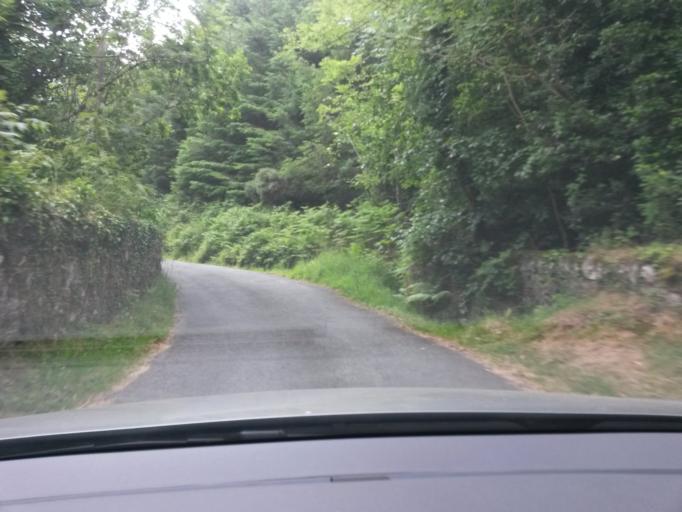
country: IE
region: Leinster
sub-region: Wicklow
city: Enniskerry
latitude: 53.1667
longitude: -6.2303
